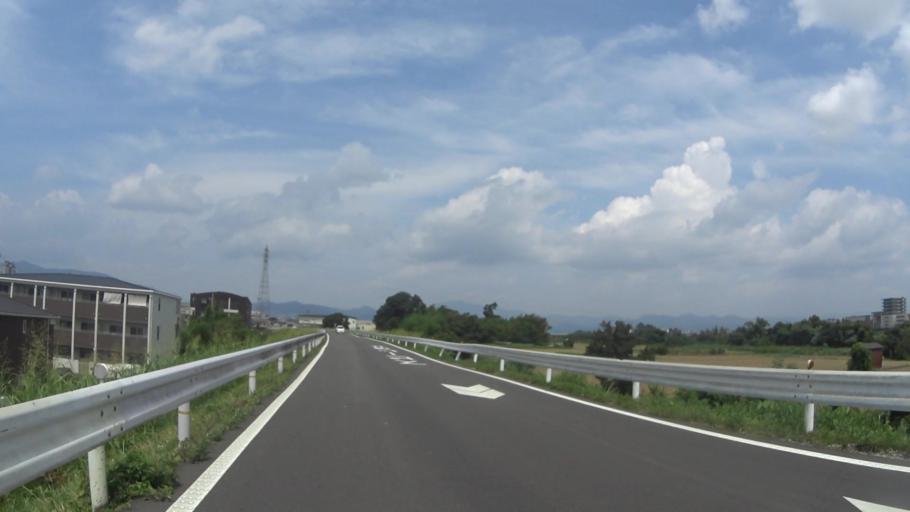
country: JP
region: Kyoto
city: Muko
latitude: 34.9495
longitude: 135.7319
